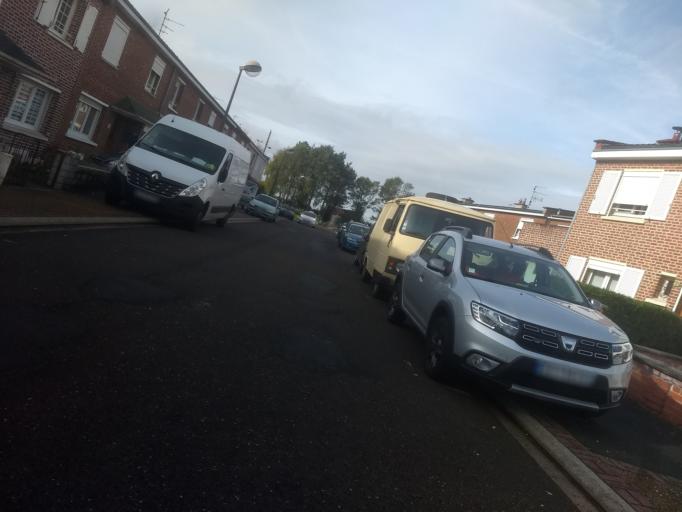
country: FR
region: Nord-Pas-de-Calais
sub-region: Departement du Pas-de-Calais
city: Anzin-Saint-Aubin
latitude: 50.2940
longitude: 2.7420
